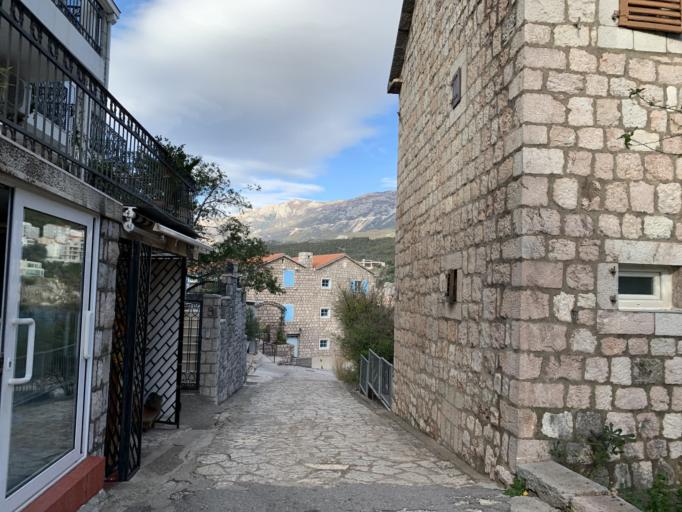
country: ME
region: Budva
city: Budva
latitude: 42.2667
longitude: 18.8916
